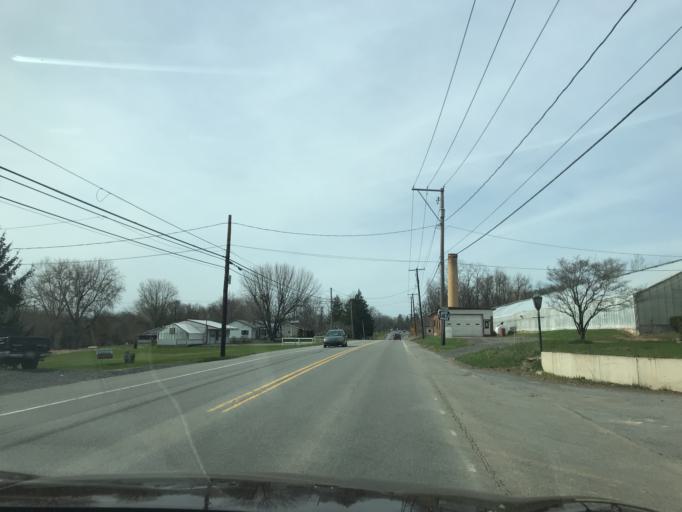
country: US
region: Pennsylvania
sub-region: Northumberland County
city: Northumberland
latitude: 40.9140
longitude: -76.8400
